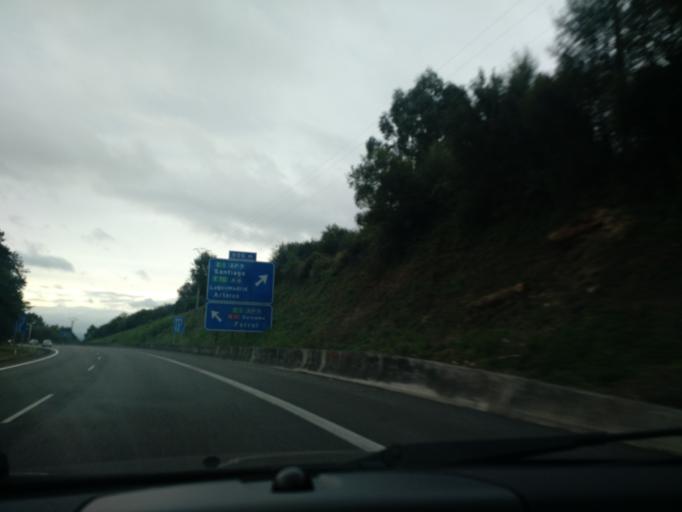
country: ES
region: Galicia
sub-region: Provincia da Coruna
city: Oleiros
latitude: 43.2900
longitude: -8.2950
